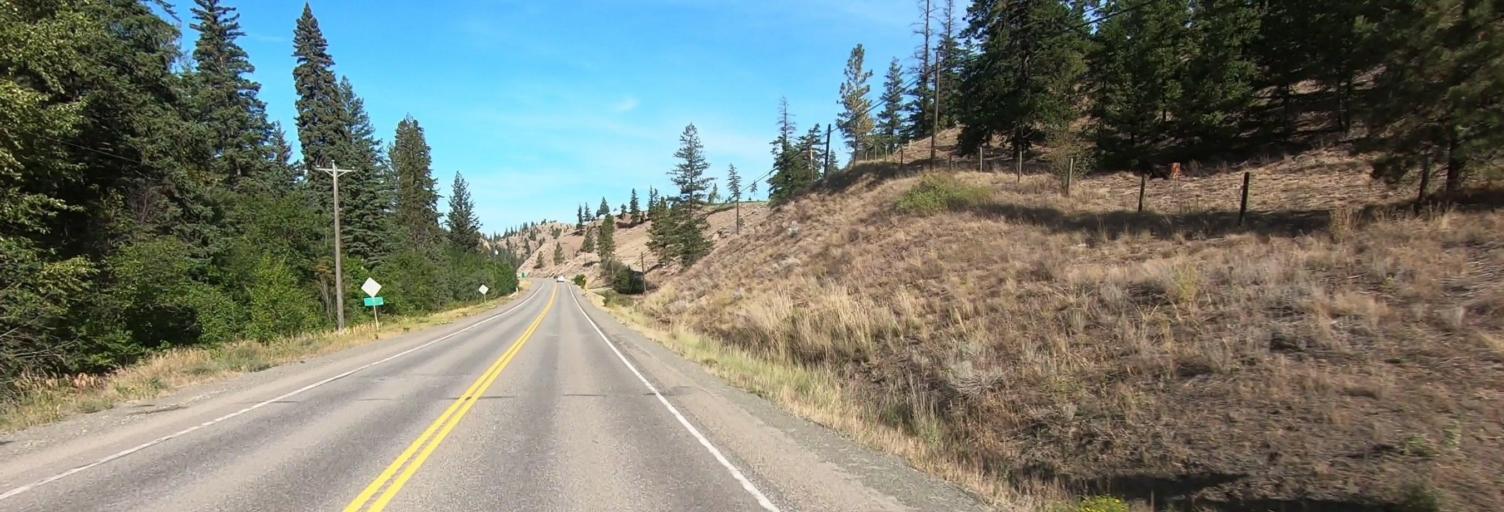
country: CA
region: British Columbia
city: Kamloops
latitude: 50.6690
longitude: -120.5654
